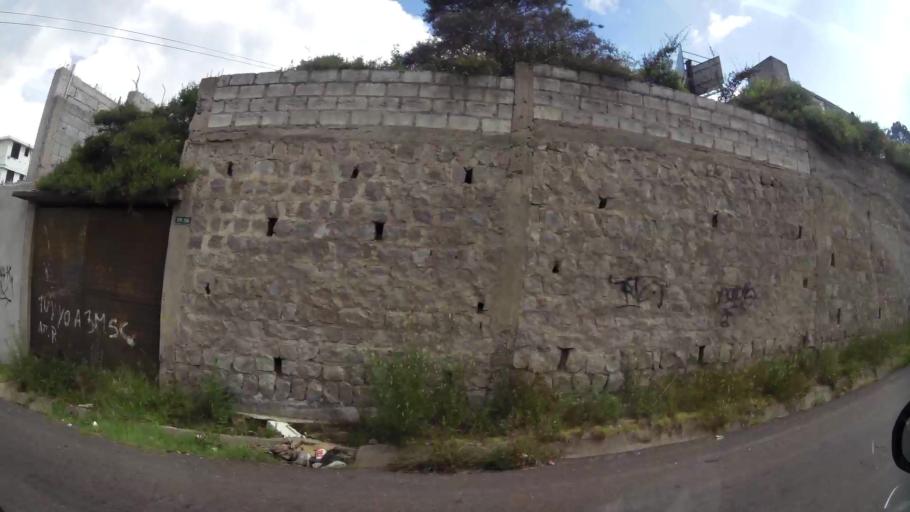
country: EC
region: Pichincha
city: Quito
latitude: -0.0964
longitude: -78.4652
